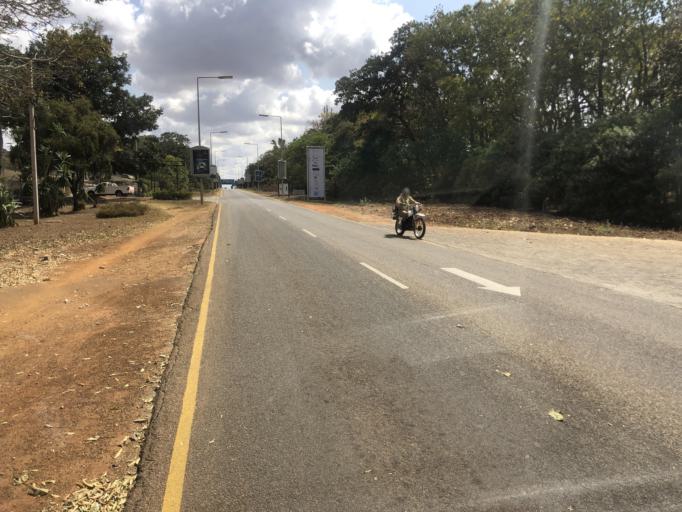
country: MW
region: Central Region
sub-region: Lilongwe District
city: Lilongwe
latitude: -13.7844
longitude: 33.7872
